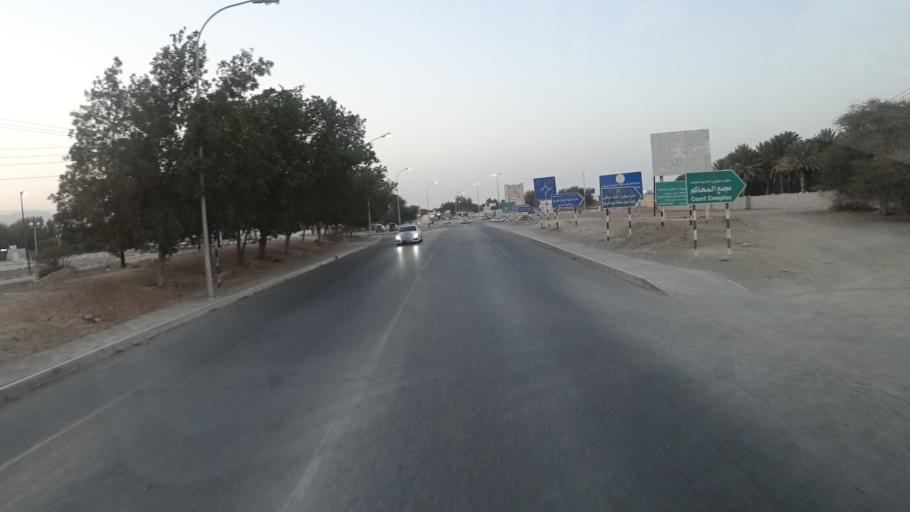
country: OM
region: Ash Sharqiyah
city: Sur
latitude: 22.5459
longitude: 59.4825
